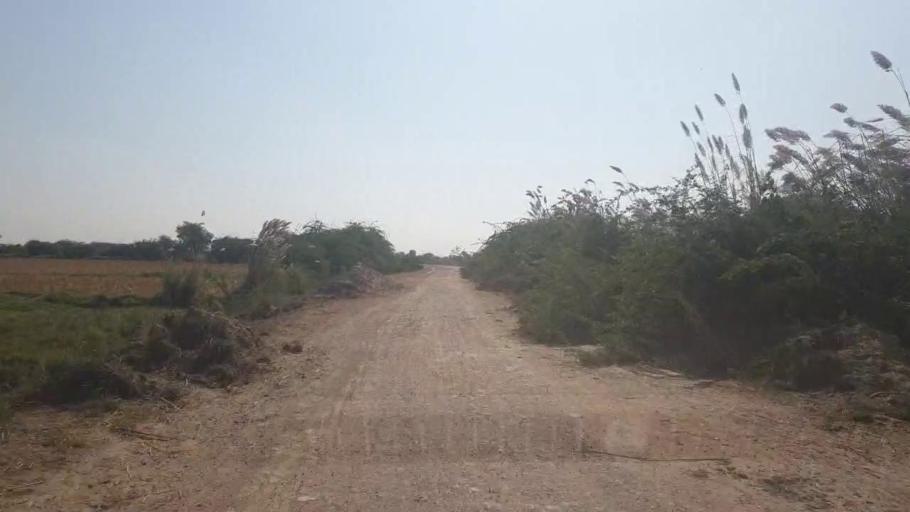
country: PK
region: Sindh
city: Badin
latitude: 24.5659
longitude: 68.8456
